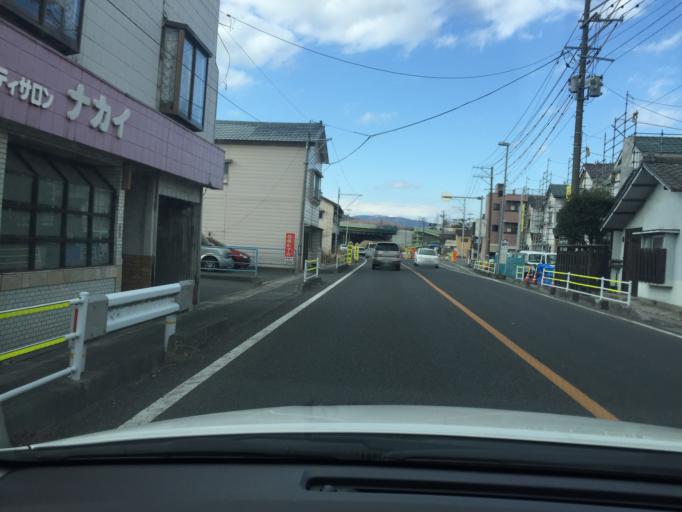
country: JP
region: Fukushima
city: Iwaki
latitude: 37.0078
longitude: 140.8503
